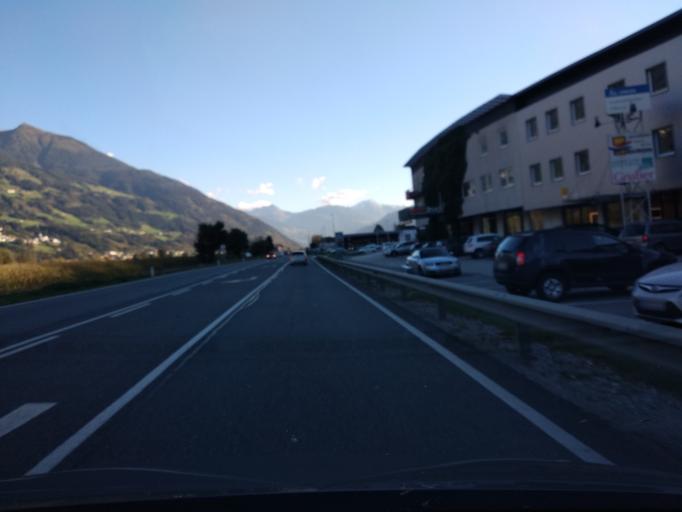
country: AT
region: Tyrol
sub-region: Politischer Bezirk Schwaz
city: Schlitters
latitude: 47.3677
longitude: 11.8496
